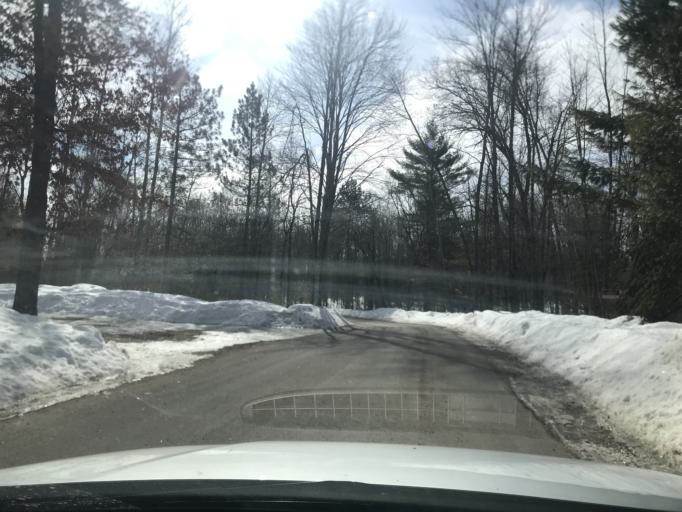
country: US
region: Wisconsin
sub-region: Menominee County
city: Legend Lake
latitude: 45.1143
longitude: -88.4438
